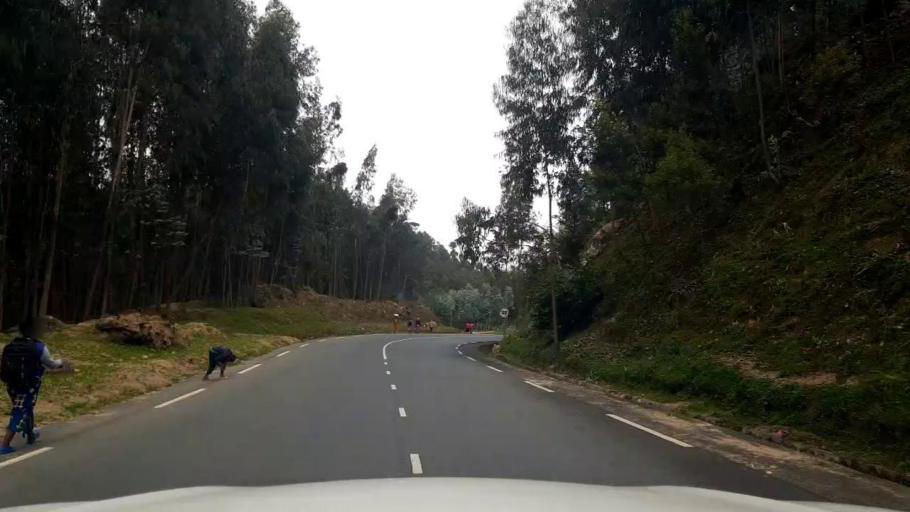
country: RW
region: Northern Province
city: Musanze
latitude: -1.6799
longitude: 29.5155
